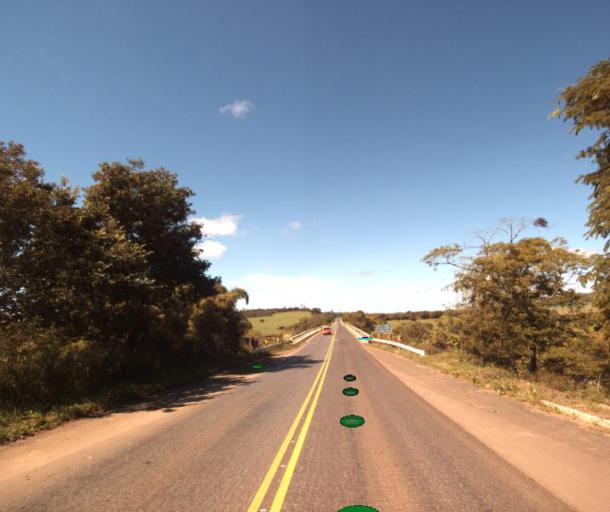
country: BR
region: Goias
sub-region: Ceres
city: Ceres
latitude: -15.1791
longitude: -49.5450
